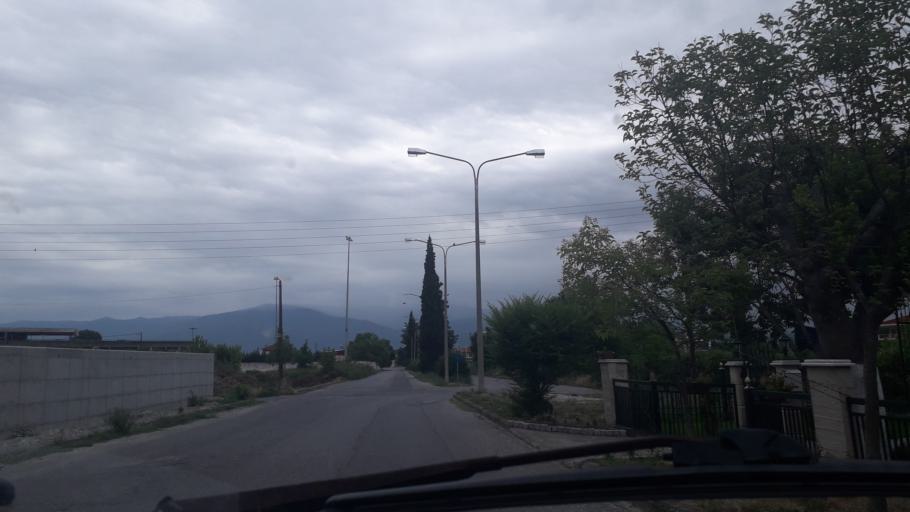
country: GR
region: Central Macedonia
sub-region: Nomos Pellis
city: Aridaia
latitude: 40.9679
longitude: 22.0632
